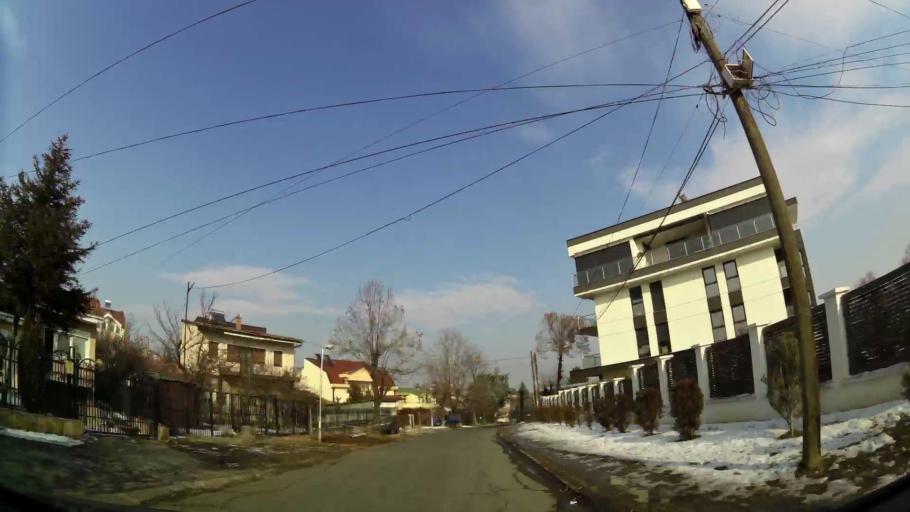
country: MK
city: Creshevo
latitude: 42.0055
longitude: 21.4970
